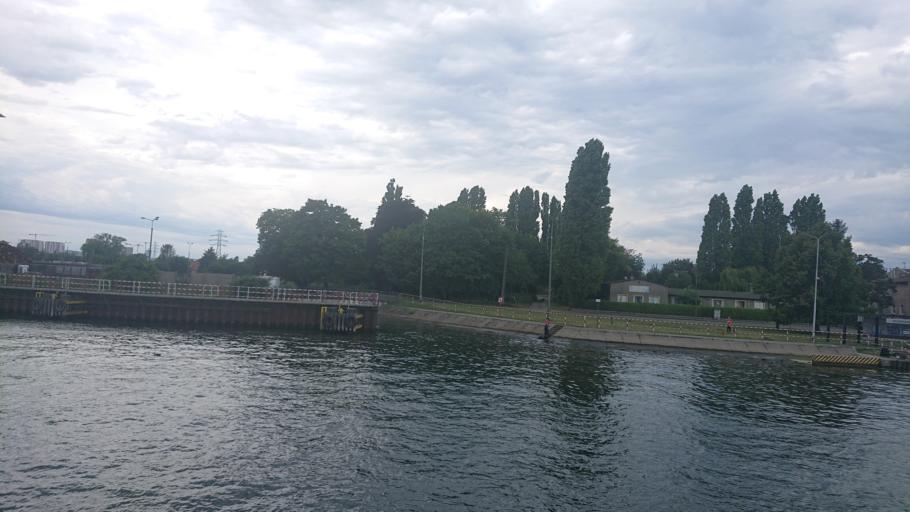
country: PL
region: Pomeranian Voivodeship
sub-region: Gdansk
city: Gdansk
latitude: 54.3938
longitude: 18.6734
